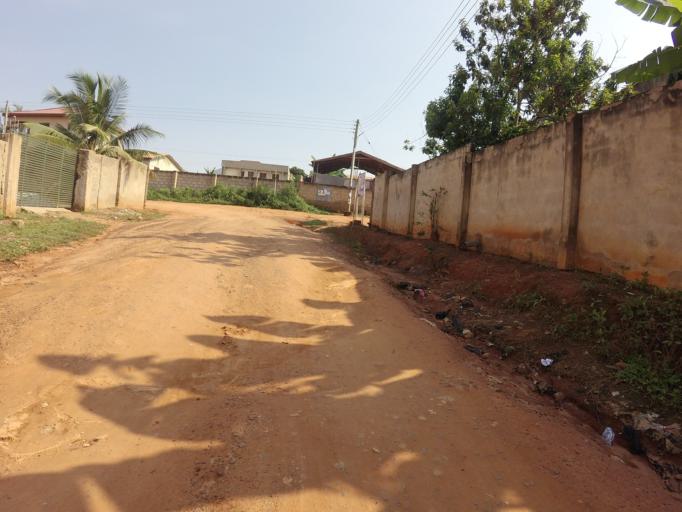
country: GH
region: Greater Accra
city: Gbawe
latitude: 5.6232
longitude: -0.3099
